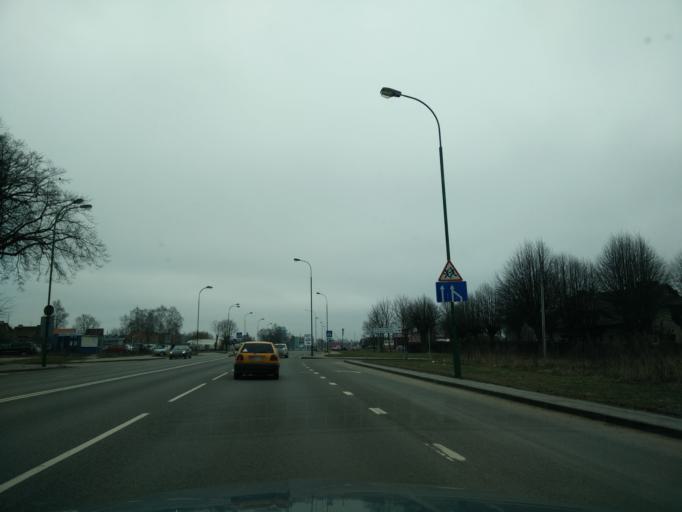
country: LT
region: Klaipedos apskritis
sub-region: Klaipeda
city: Klaipeda
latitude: 55.6928
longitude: 21.1420
